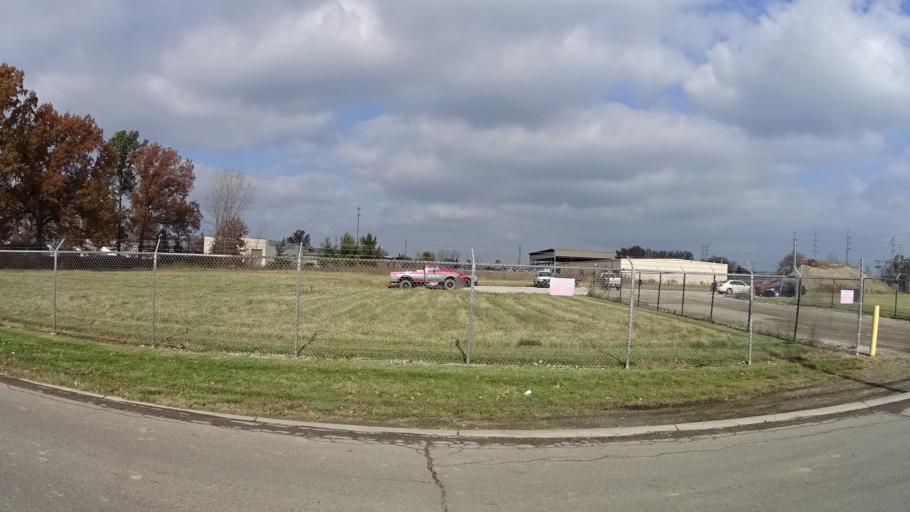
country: US
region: Ohio
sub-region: Lorain County
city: Elyria
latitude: 41.3687
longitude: -82.0794
